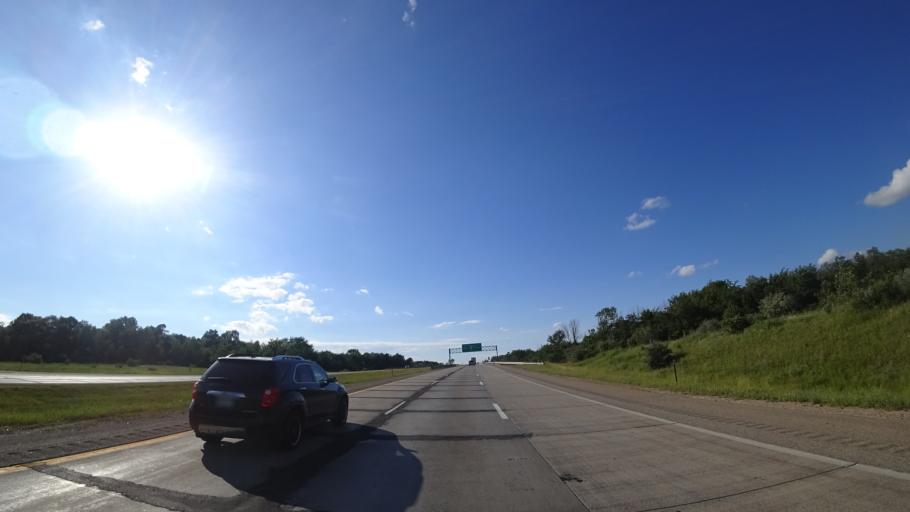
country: US
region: Michigan
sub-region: Ottawa County
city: Jenison
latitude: 42.8505
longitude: -85.8090
